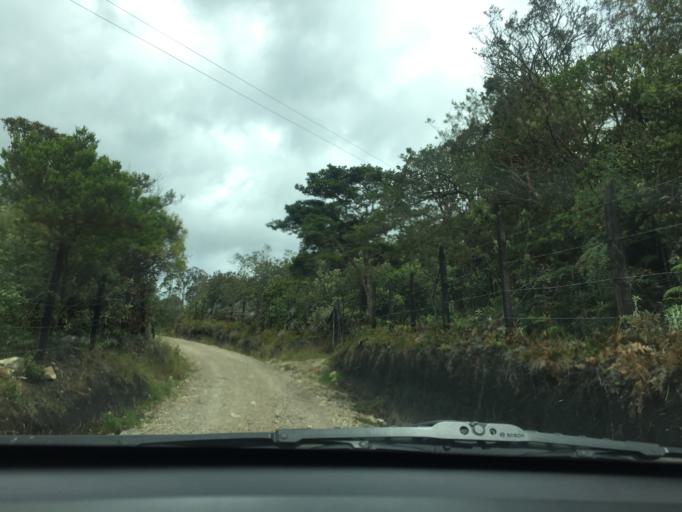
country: CO
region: Cundinamarca
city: Tocancipa
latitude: 4.9604
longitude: -73.8850
